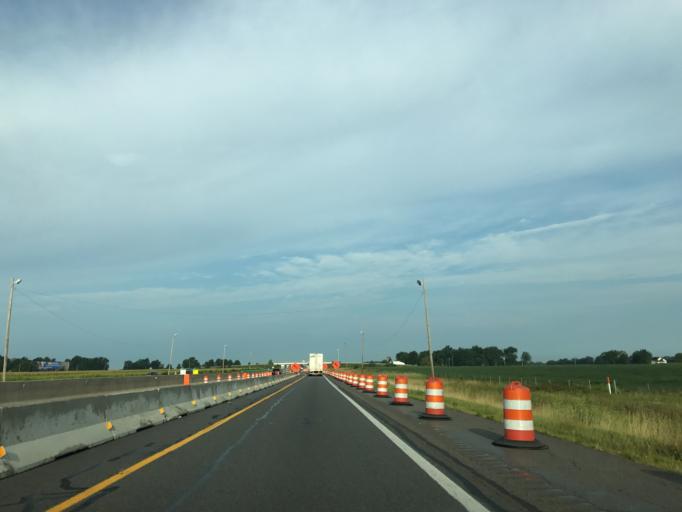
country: US
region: Ohio
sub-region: Huron County
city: Monroeville
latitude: 41.3362
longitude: -82.7138
